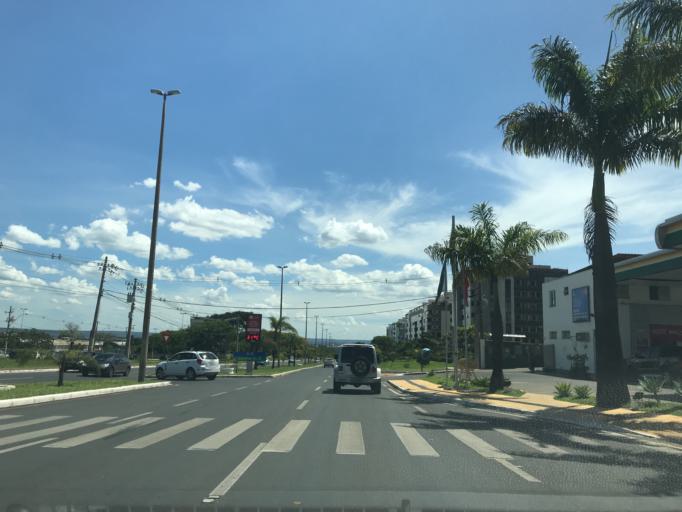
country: BR
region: Federal District
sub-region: Brasilia
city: Brasilia
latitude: -15.7877
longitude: -47.9150
